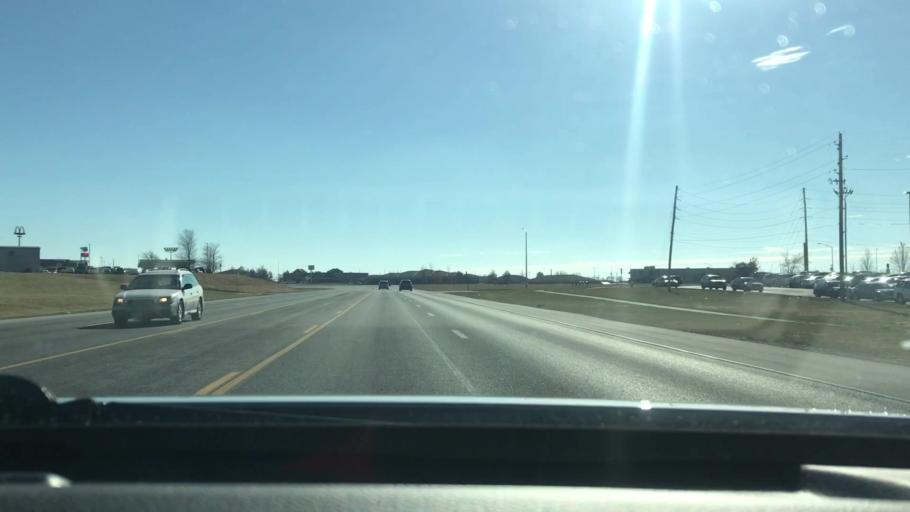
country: US
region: Missouri
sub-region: Platte County
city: Platte City
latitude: 39.3576
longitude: -94.7694
